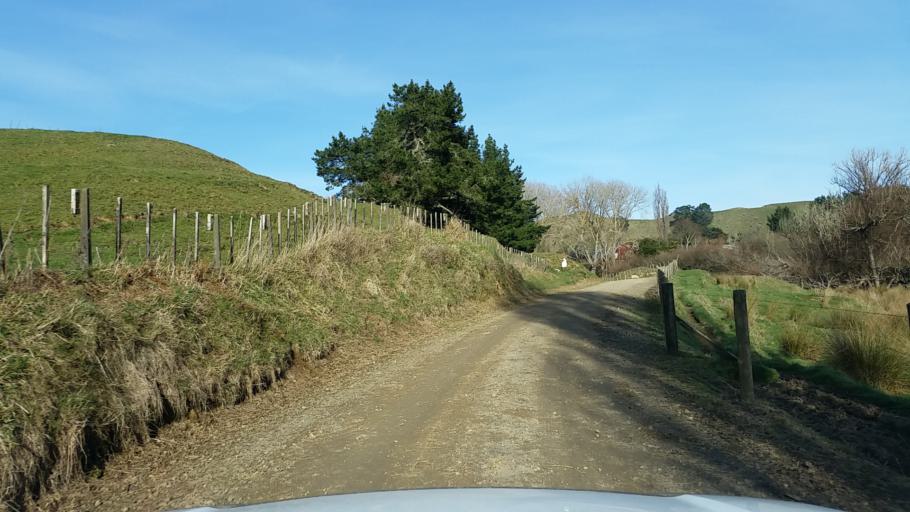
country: NZ
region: Taranaki
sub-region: South Taranaki District
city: Eltham
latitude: -39.3173
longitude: 174.5334
